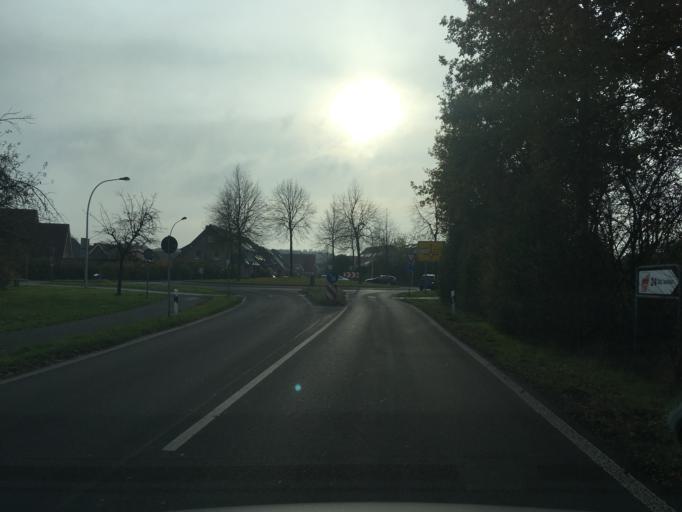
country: DE
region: North Rhine-Westphalia
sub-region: Regierungsbezirk Munster
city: Velen
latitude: 51.8952
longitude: 6.9730
